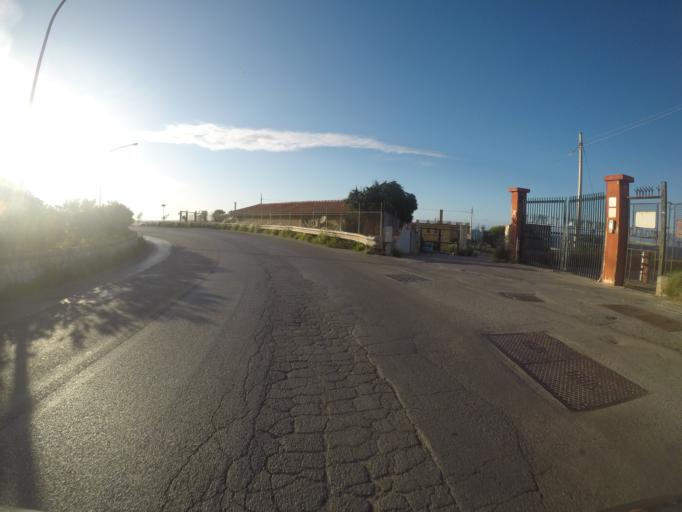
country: IT
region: Sicily
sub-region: Palermo
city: Isola delle Femmine
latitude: 38.2015
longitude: 13.2686
